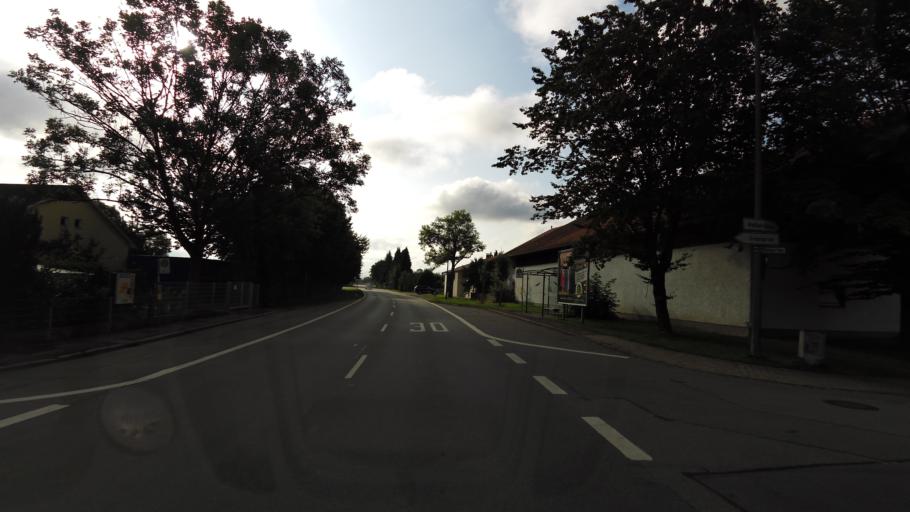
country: DE
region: Bavaria
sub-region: Lower Bavaria
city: Straubing
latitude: 48.9068
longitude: 12.5616
